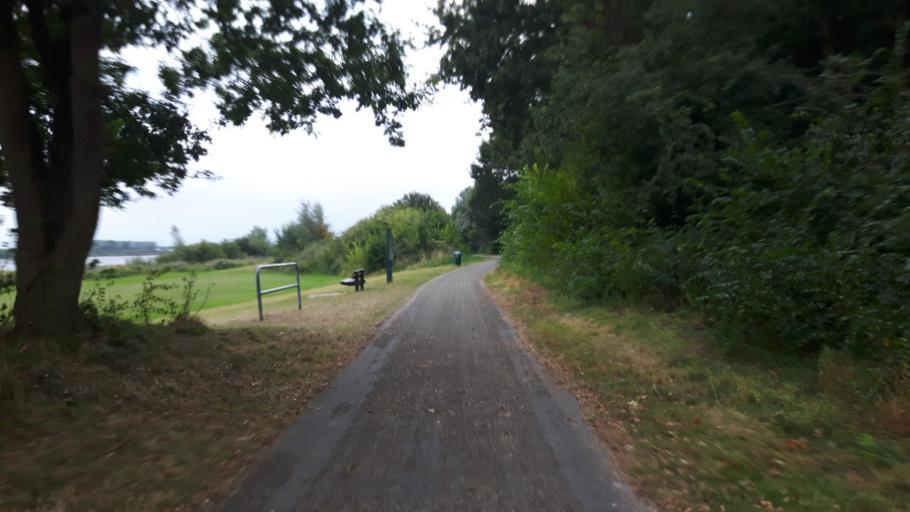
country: NL
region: South Holland
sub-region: Gemeente Noordwijkerhout
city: Noordwijkerhout
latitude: 52.2858
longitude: 4.5089
